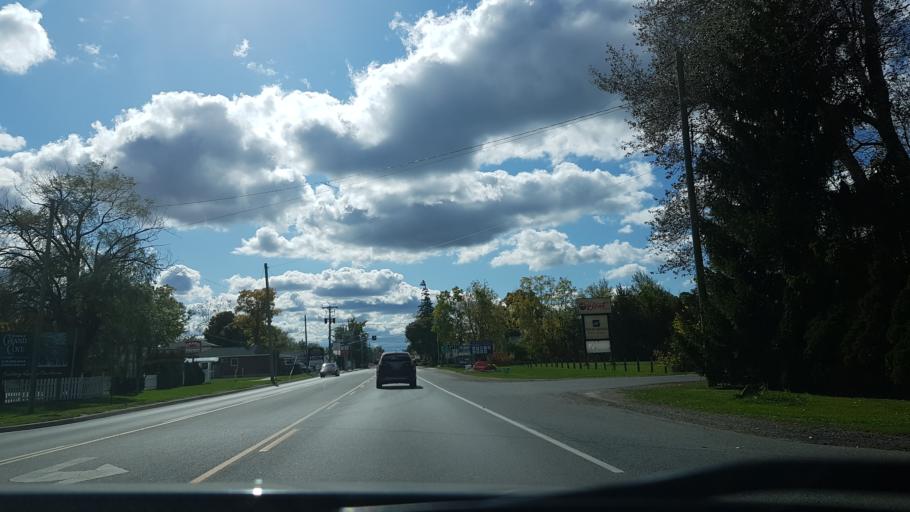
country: CA
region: Ontario
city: Bluewater
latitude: 43.3165
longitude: -81.7535
